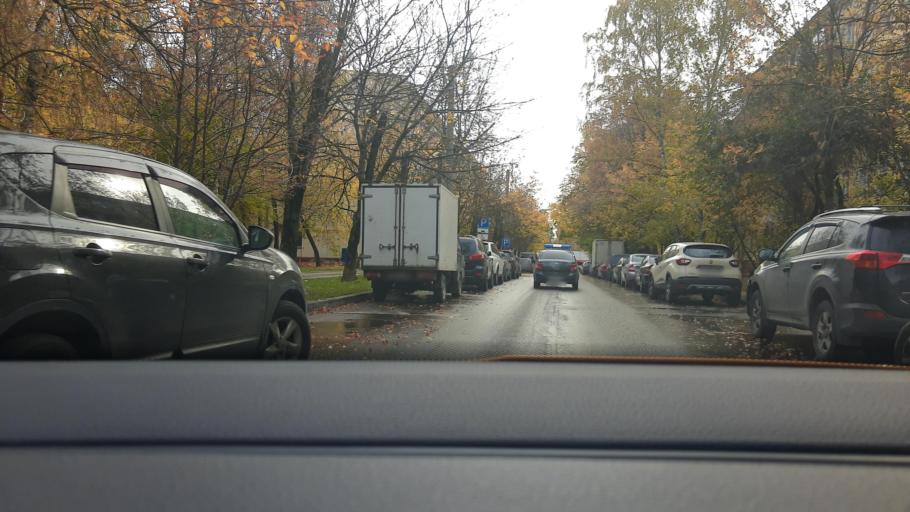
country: RU
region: Moskovskaya
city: Fili
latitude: 55.7333
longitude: 37.4778
